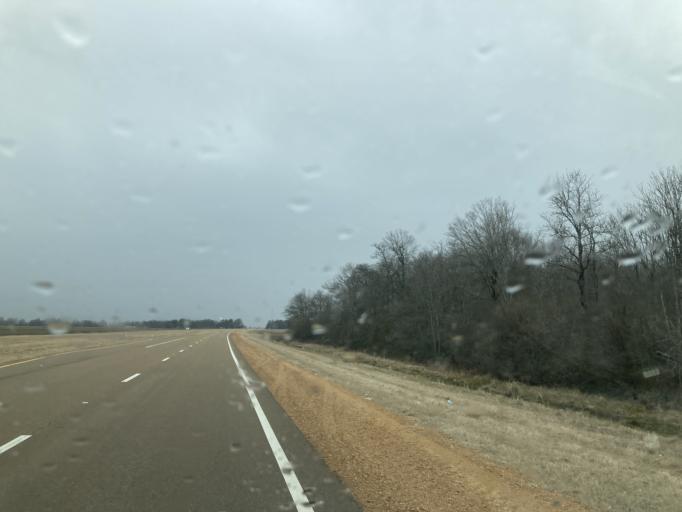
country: US
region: Mississippi
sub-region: Humphreys County
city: Belzoni
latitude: 33.0820
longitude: -90.4832
